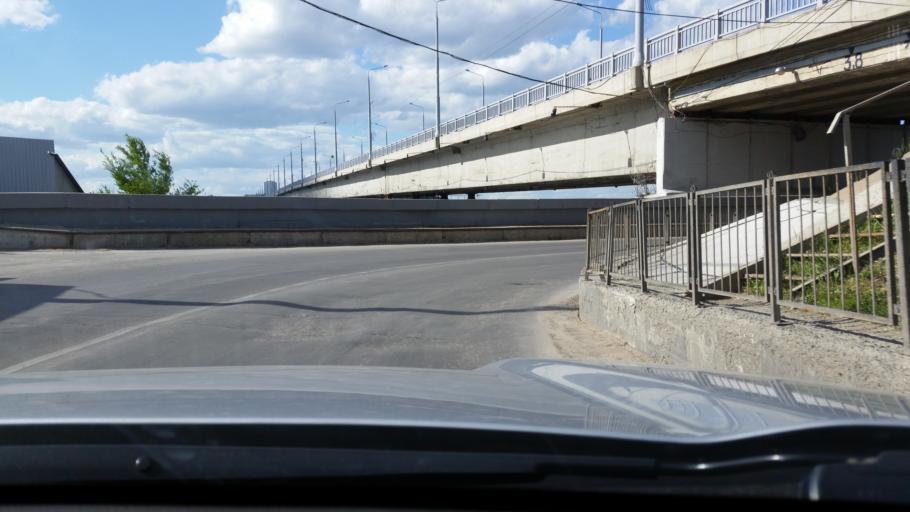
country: RU
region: Saratov
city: Engel's
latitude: 51.5056
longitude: 46.0777
